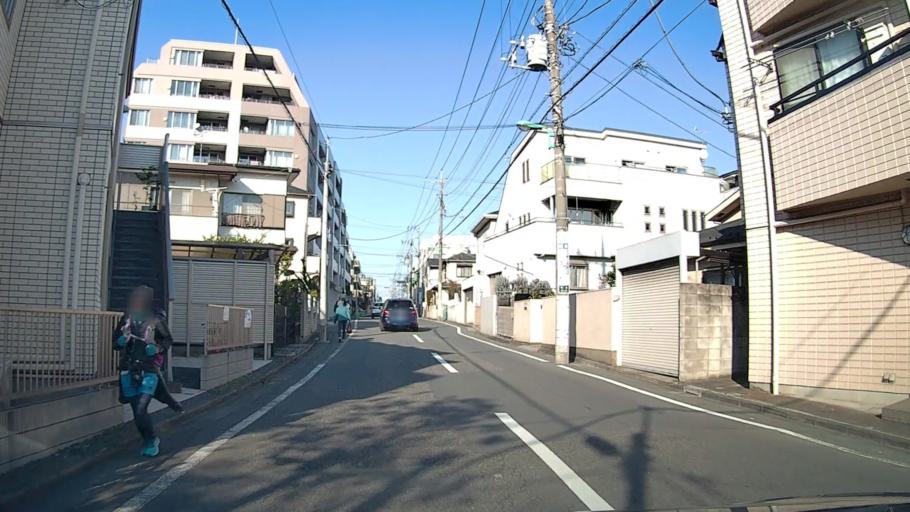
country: JP
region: Saitama
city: Wako
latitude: 35.7463
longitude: 139.6488
